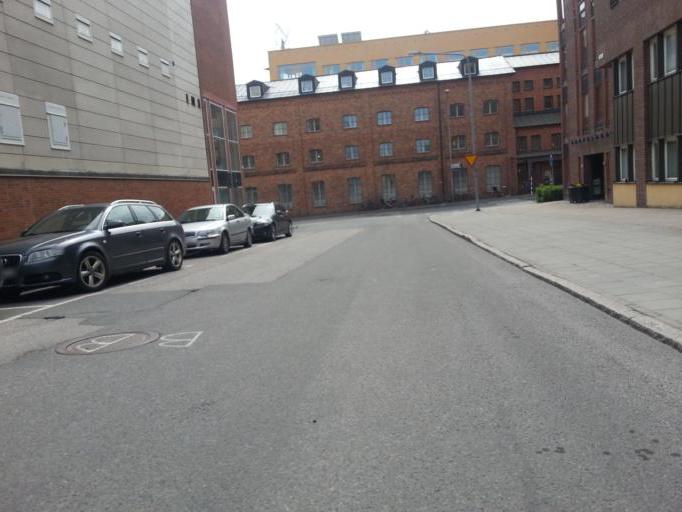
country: SE
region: Joenkoeping
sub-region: Jonkopings Kommun
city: Jonkoping
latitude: 57.7793
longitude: 14.1652
